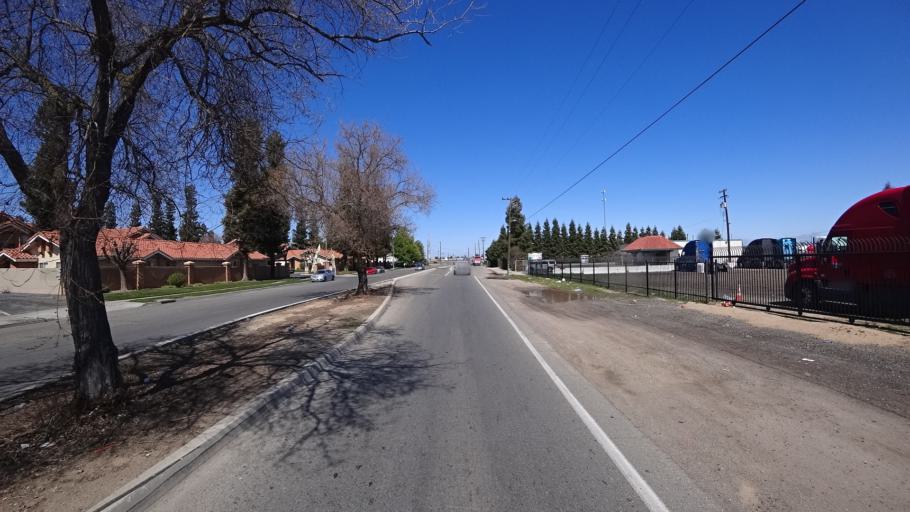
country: US
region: California
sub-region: Fresno County
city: West Park
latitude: 36.7736
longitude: -119.8443
